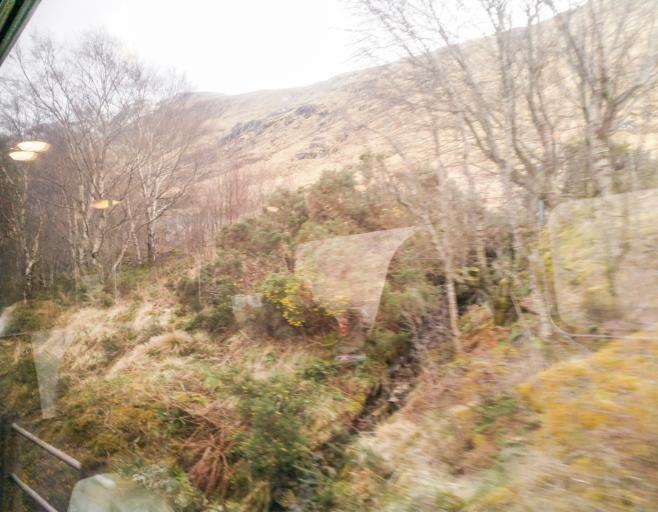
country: GB
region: Scotland
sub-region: Highland
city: Spean Bridge
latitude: 56.8165
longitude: -4.7146
